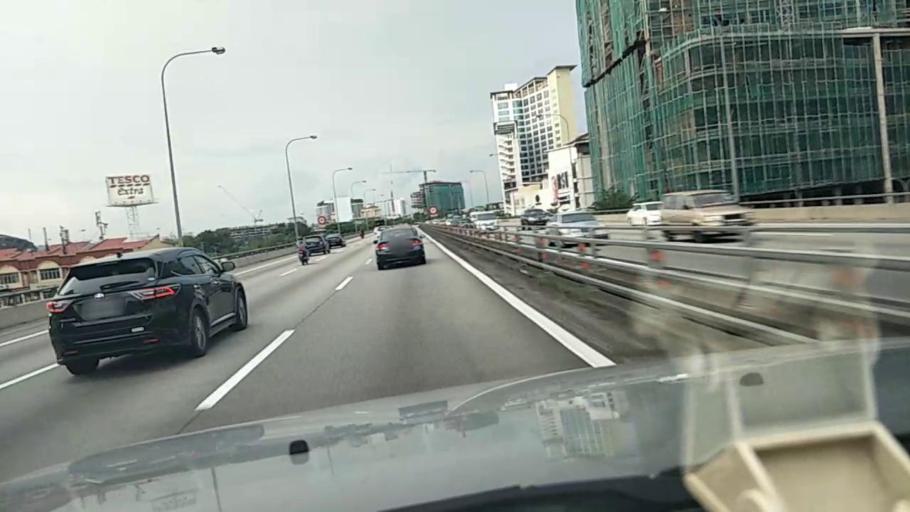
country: MY
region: Selangor
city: Shah Alam
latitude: 3.0754
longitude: 101.5526
